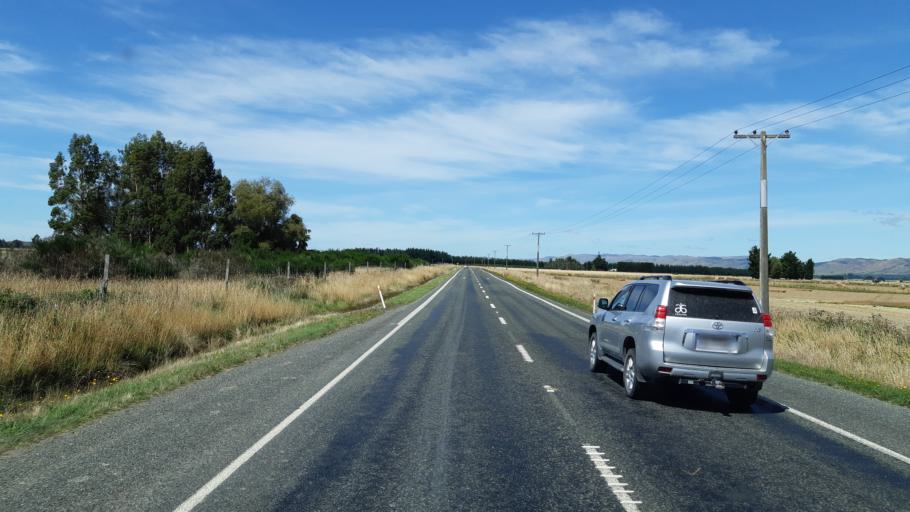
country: NZ
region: Southland
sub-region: Southland District
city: Winton
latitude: -45.7754
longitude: 168.4708
